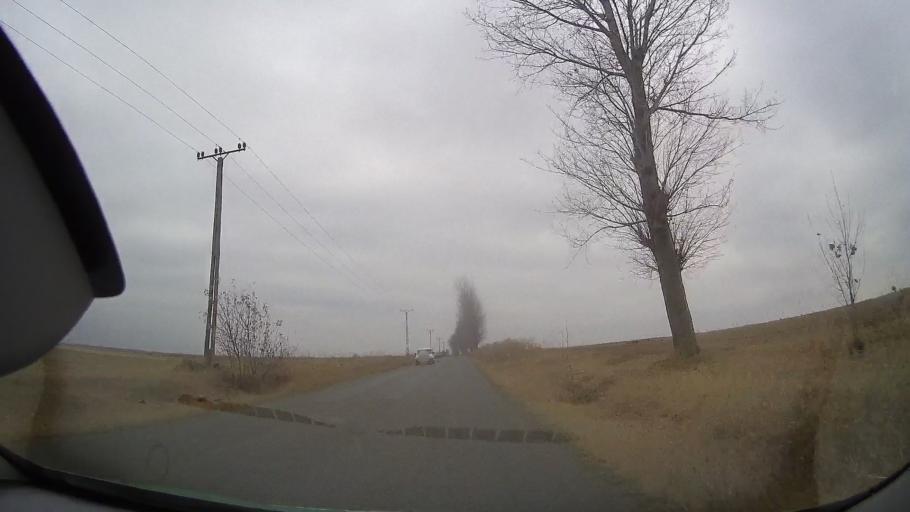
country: RO
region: Buzau
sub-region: Comuna Pogoanele
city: Pogoanele
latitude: 44.9468
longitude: 27.0109
